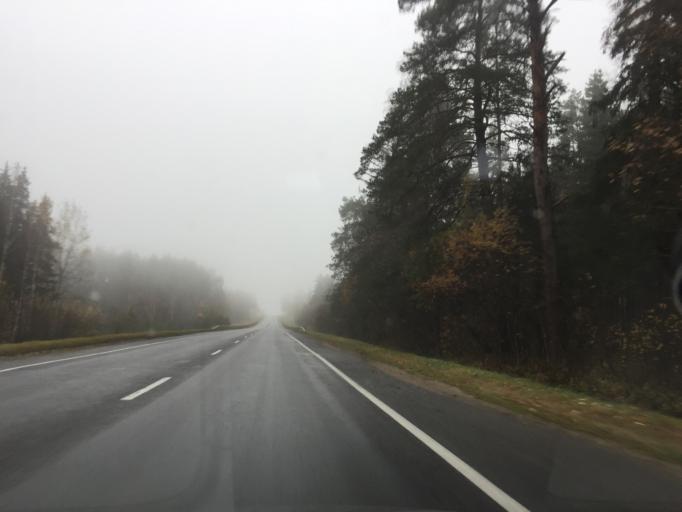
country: BY
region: Mogilev
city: Palykavichy Pyershyya
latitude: 54.0252
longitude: 30.4638
